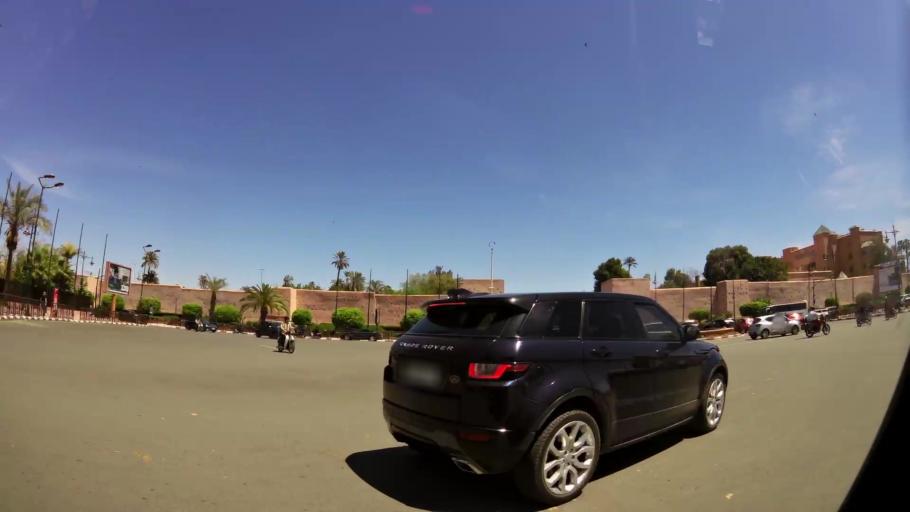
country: MA
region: Marrakech-Tensift-Al Haouz
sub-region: Marrakech
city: Marrakesh
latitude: 31.6216
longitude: -7.9996
